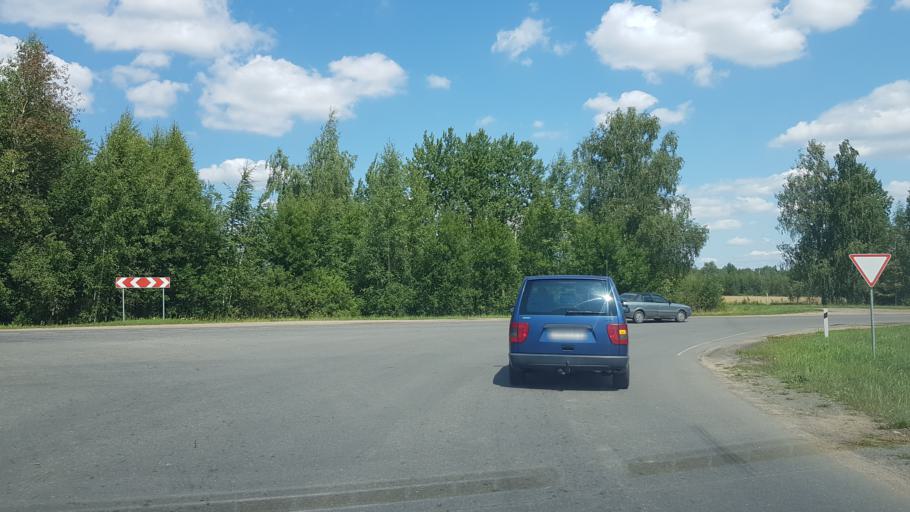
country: BY
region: Mogilev
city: Babruysk
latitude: 53.1060
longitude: 29.1684
